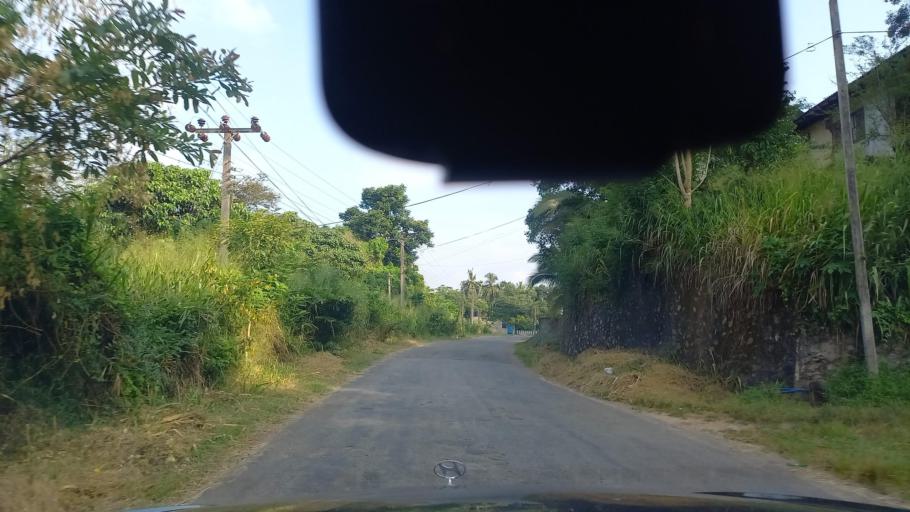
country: LK
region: Central
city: Gampola
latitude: 7.2266
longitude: 80.6038
